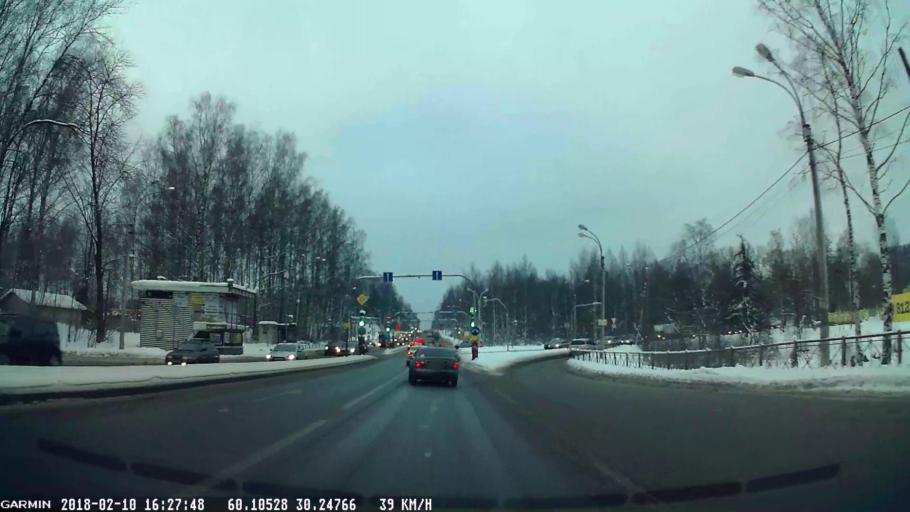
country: RU
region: St.-Petersburg
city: Pargolovo
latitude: 60.1055
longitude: 30.2475
